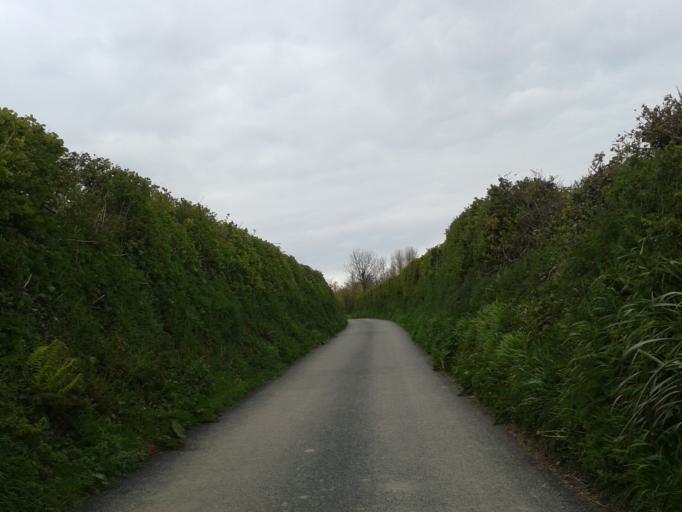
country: GB
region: England
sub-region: Devon
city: Braunton
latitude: 51.1356
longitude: -4.2186
